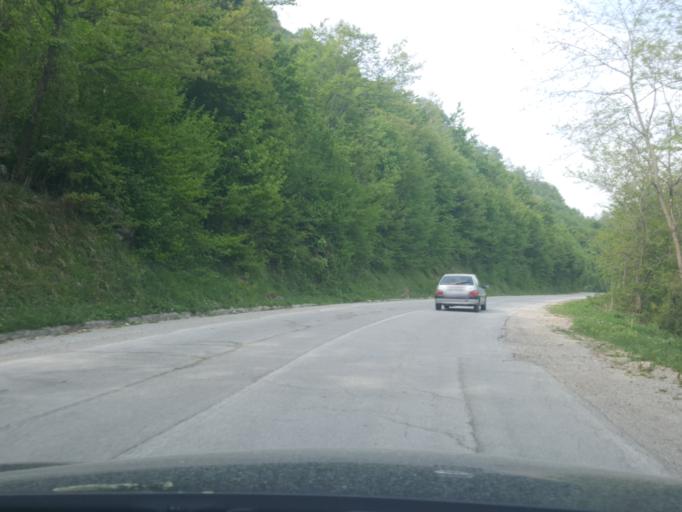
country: RS
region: Central Serbia
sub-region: Zlatiborski Okrug
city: Bajina Basta
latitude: 44.0942
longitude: 19.6631
